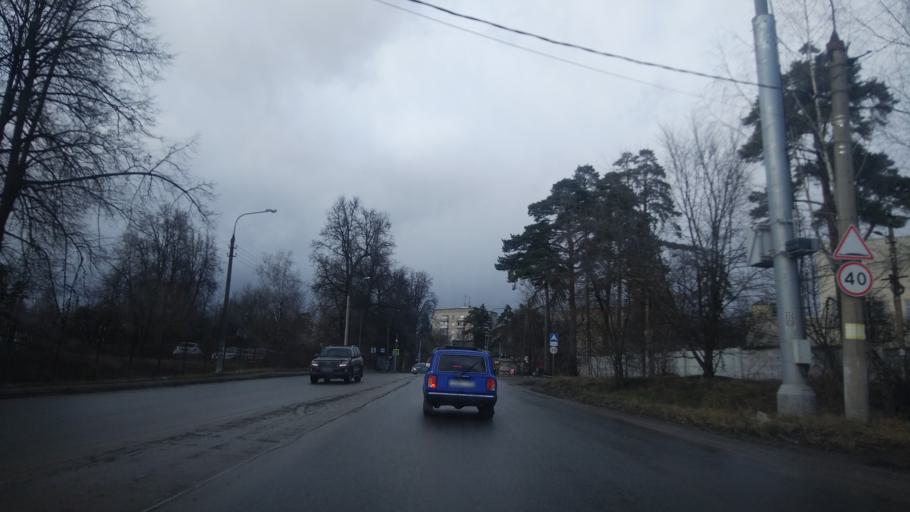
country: RU
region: Moskovskaya
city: Mamontovka
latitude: 56.0047
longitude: 37.8300
